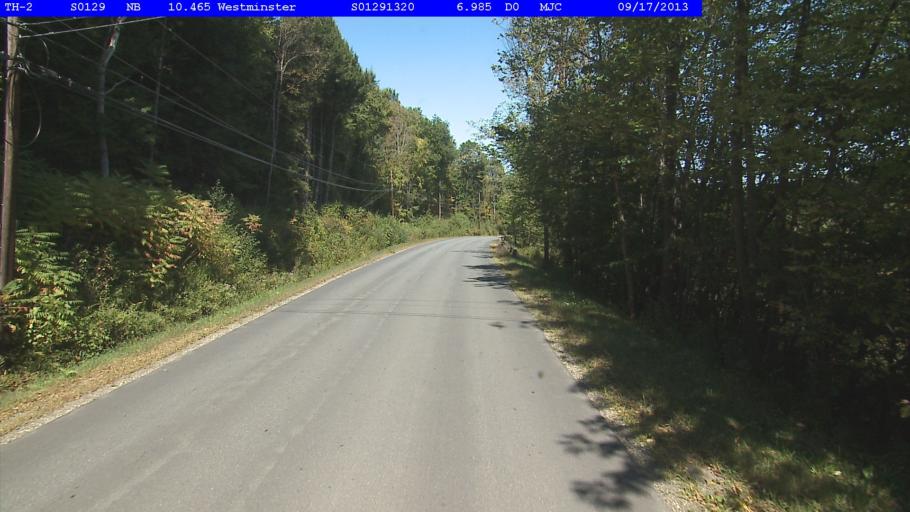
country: US
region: Vermont
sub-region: Windham County
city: Rockingham
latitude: 43.1149
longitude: -72.5360
